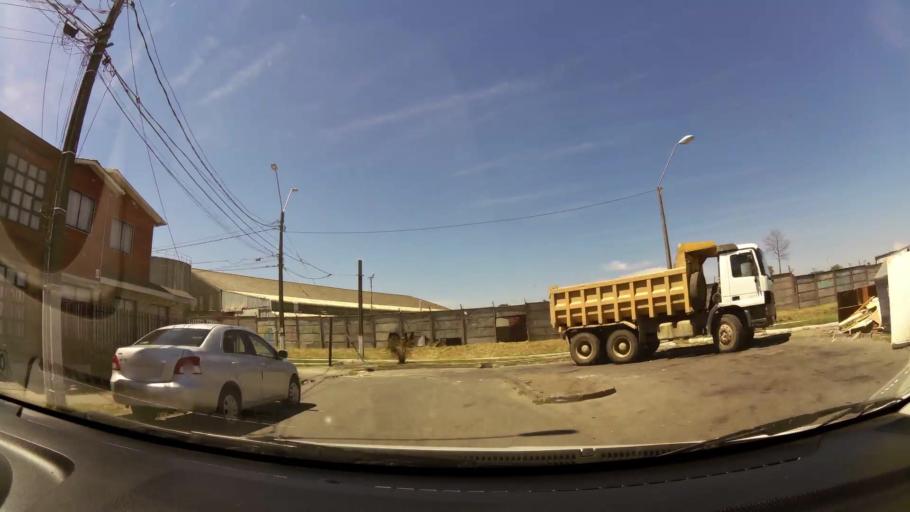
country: CL
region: Biobio
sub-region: Provincia de Concepcion
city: Talcahuano
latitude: -36.7557
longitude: -73.0819
